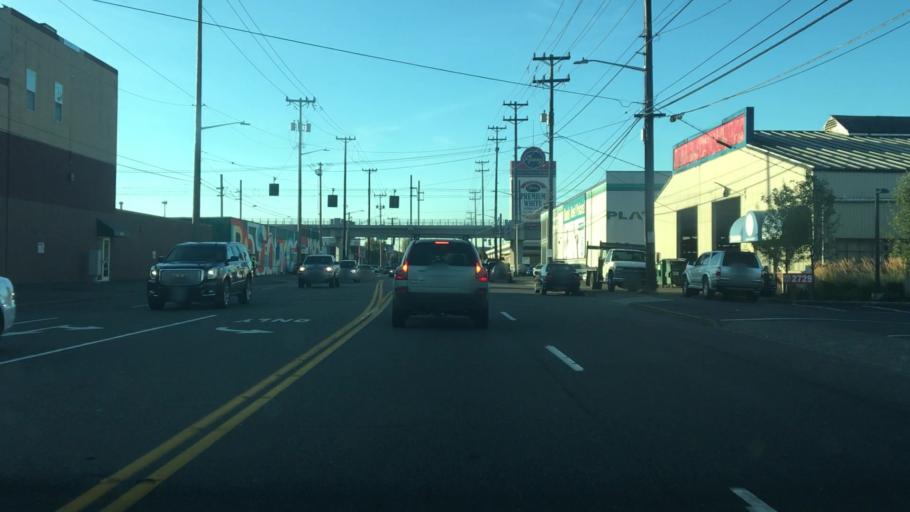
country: US
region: Washington
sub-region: King County
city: Seattle
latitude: 47.5791
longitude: -122.3261
